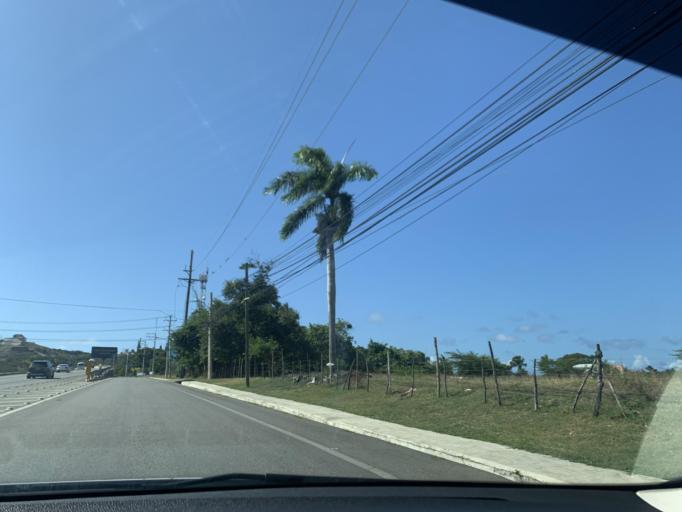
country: DO
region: Puerto Plata
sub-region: Puerto Plata
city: Puerto Plata
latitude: 19.8146
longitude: -70.7318
